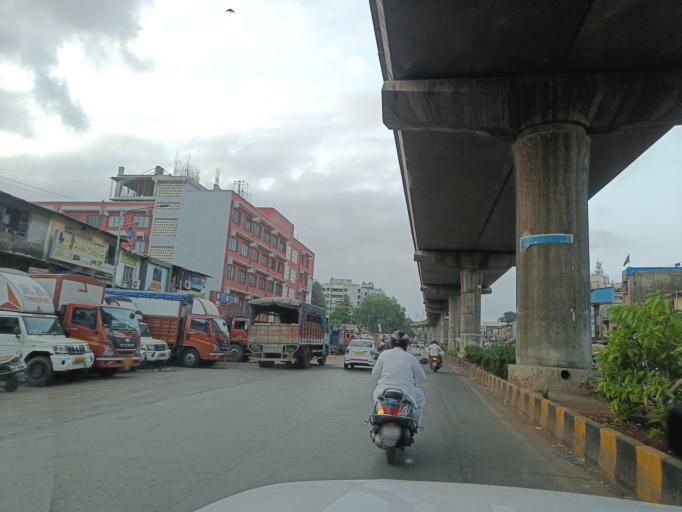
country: IN
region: Maharashtra
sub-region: Mumbai Suburban
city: Powai
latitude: 19.1005
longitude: 72.8915
